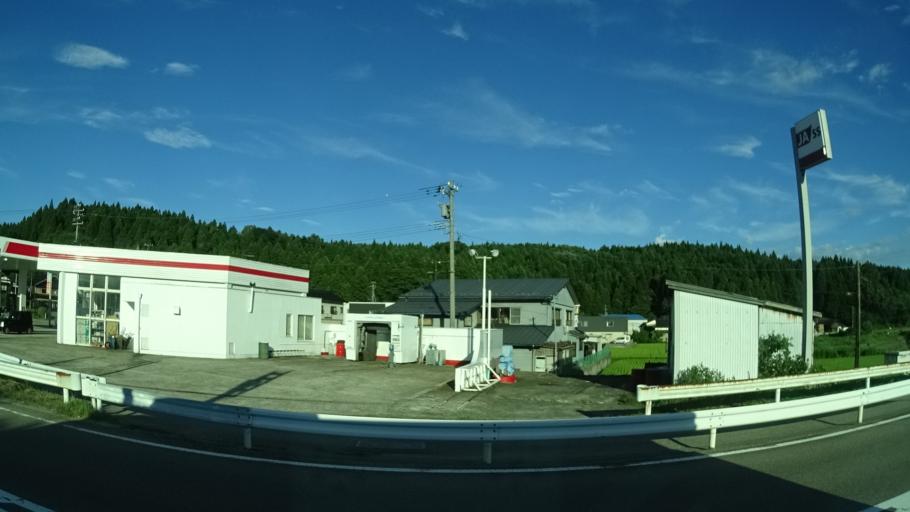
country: JP
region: Ishikawa
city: Nanao
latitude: 37.2433
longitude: 136.8990
